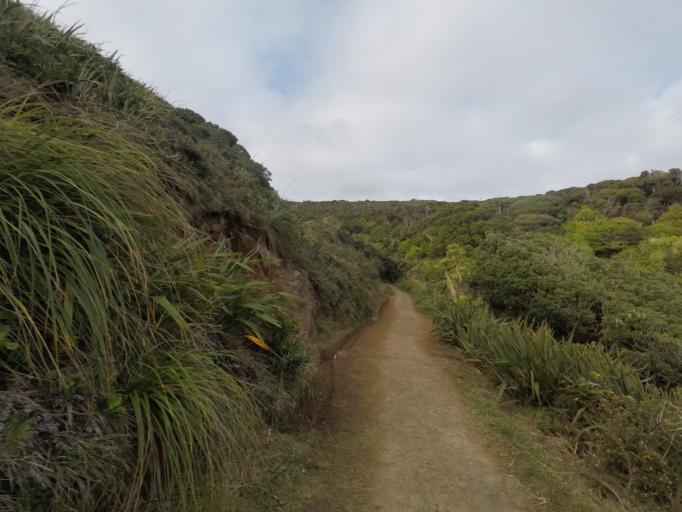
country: NZ
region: Auckland
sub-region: Auckland
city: Muriwai Beach
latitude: -36.9740
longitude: 174.4705
